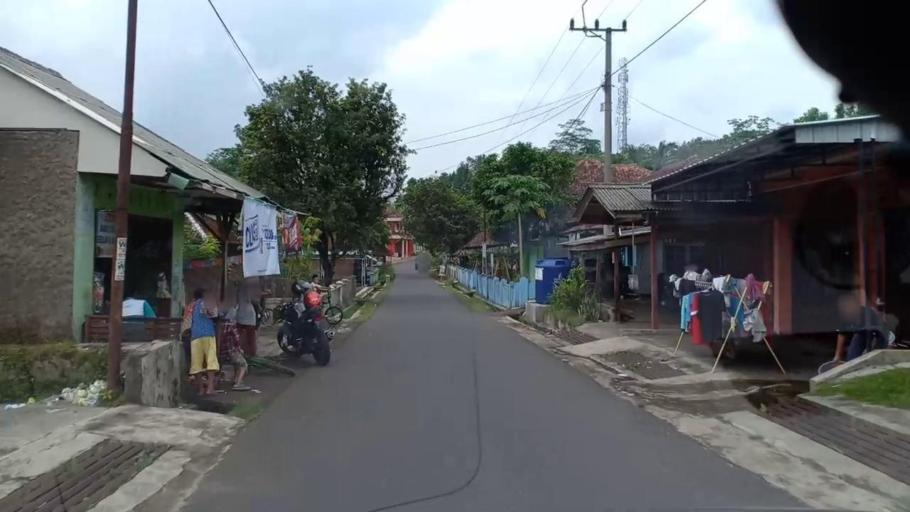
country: ID
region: West Java
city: Gerempay
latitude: -7.3377
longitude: 108.2864
